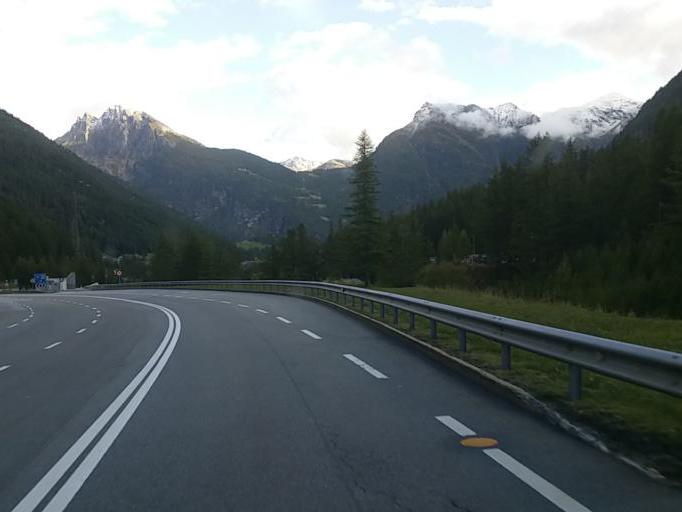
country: CH
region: Valais
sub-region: Brig District
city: Brig
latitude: 46.2035
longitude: 8.0448
